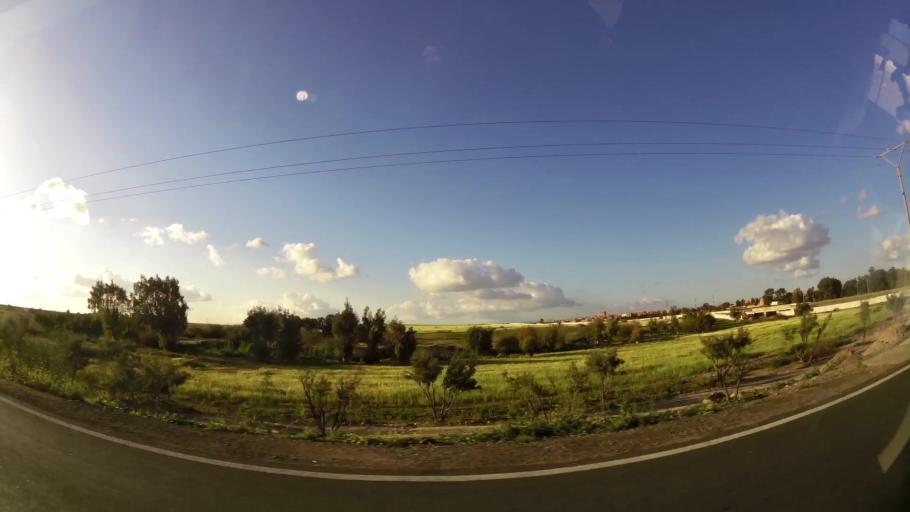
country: MA
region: Marrakech-Tensift-Al Haouz
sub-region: Kelaa-Des-Sraghna
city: Sidi Bou Othmane
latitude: 32.2282
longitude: -7.9665
